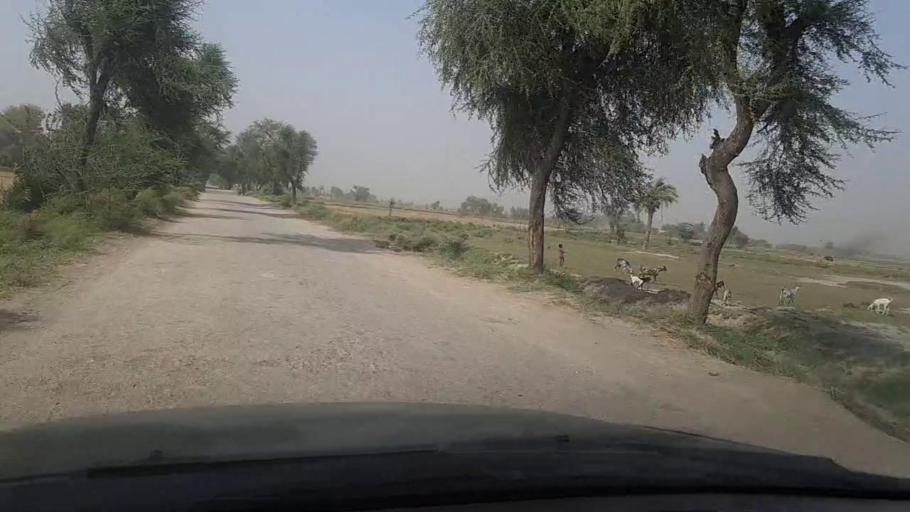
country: PK
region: Sindh
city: Shikarpur
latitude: 27.9259
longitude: 68.6145
